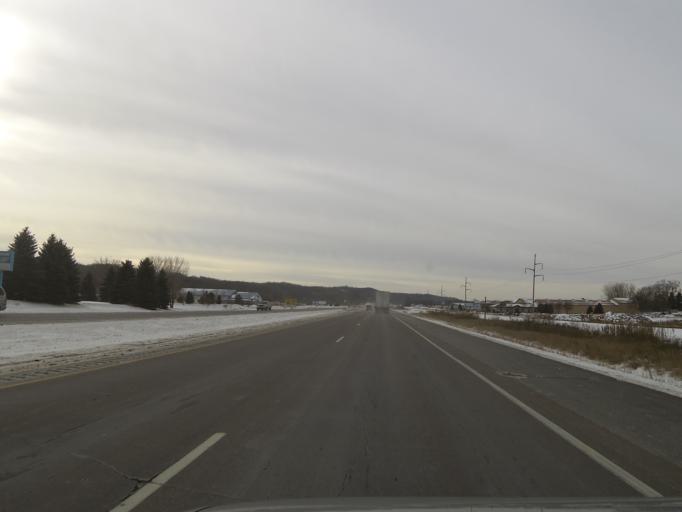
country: US
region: Minnesota
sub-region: Scott County
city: Jordan
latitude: 44.7117
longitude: -93.5904
